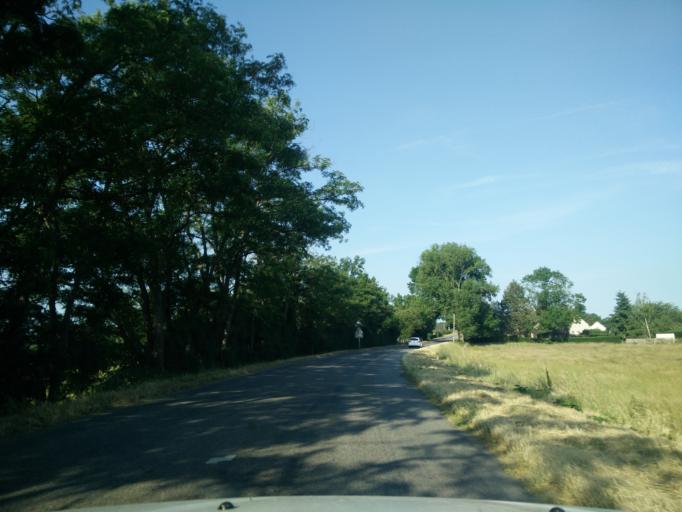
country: FR
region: Auvergne
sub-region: Departement de l'Allier
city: Toulon-sur-Allier
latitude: 46.4814
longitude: 3.3023
